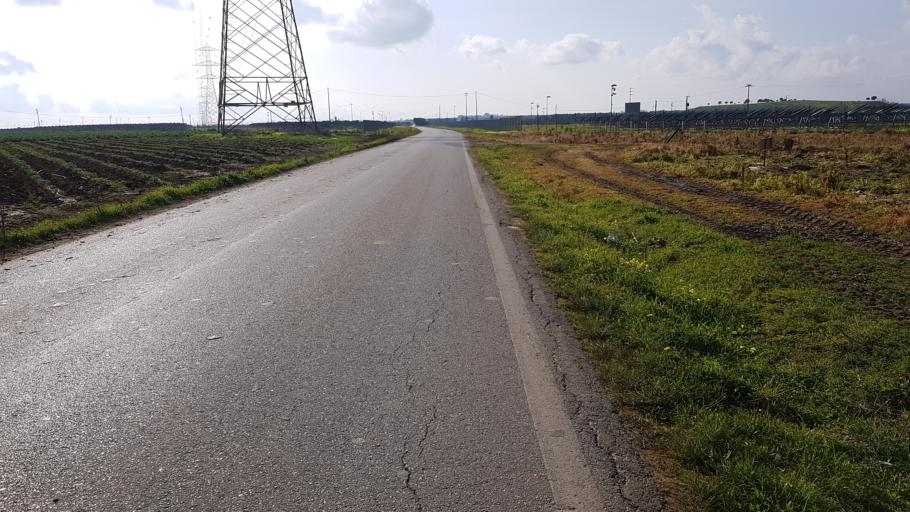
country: IT
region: Apulia
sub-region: Provincia di Brindisi
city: La Rosa
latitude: 40.5916
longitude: 17.9033
